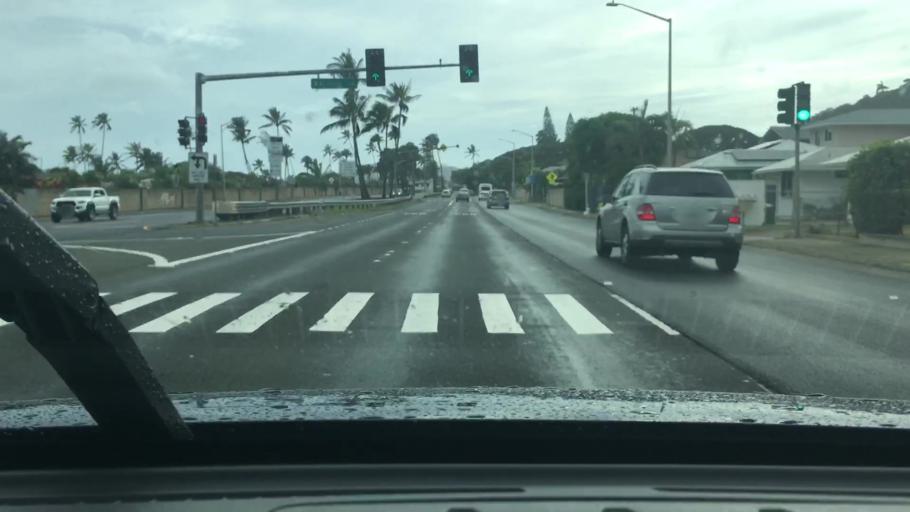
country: US
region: Hawaii
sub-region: Honolulu County
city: Waimanalo
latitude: 21.2774
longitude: -157.7573
